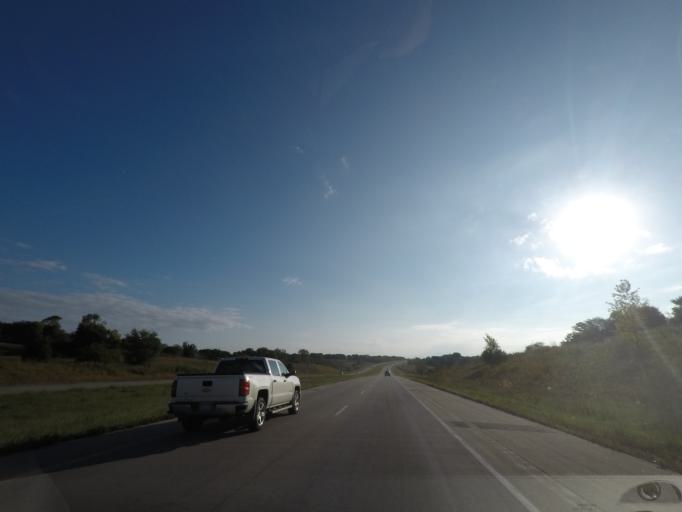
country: US
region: Iowa
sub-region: Warren County
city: Carlisle
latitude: 41.5093
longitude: -93.5592
